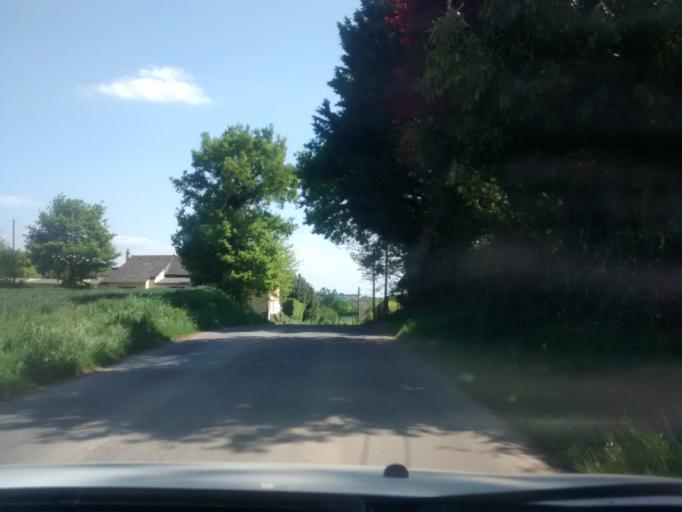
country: FR
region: Brittany
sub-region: Departement d'Ille-et-Vilaine
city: Cesson-Sevigne
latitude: 48.1384
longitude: -1.6017
